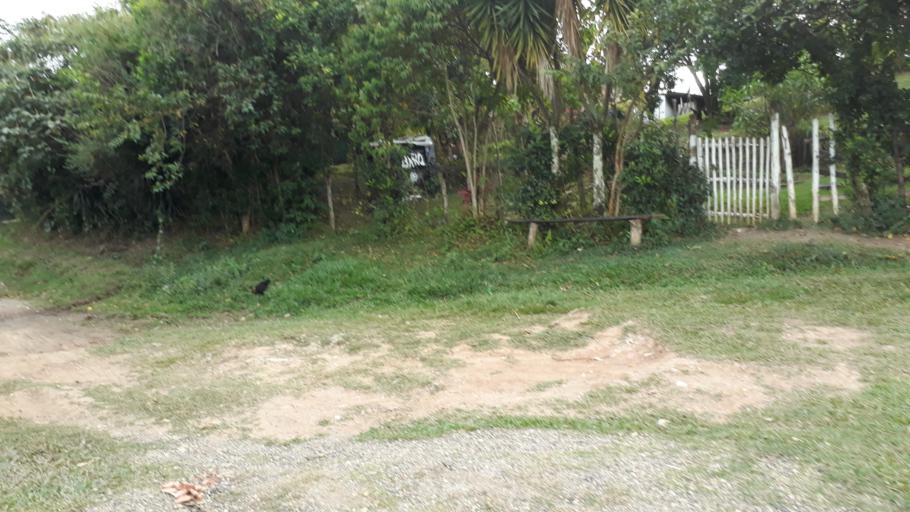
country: CO
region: Valle del Cauca
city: Jamundi
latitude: 3.2062
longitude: -76.6307
